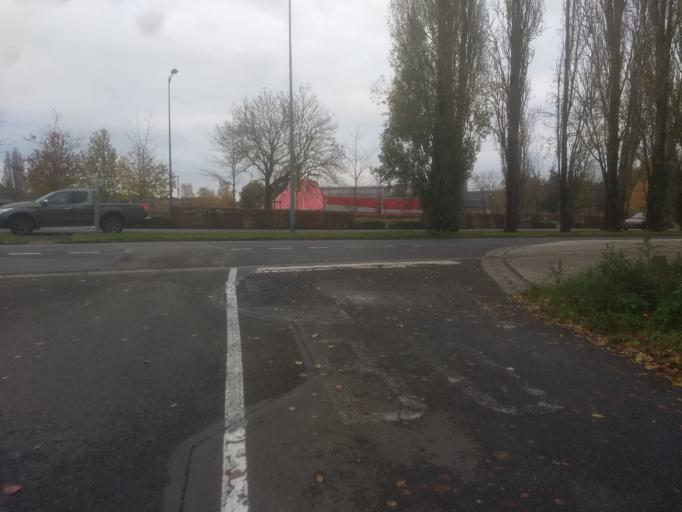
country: FR
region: Nord-Pas-de-Calais
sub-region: Departement du Pas-de-Calais
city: Achicourt
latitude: 50.2881
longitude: 2.7602
